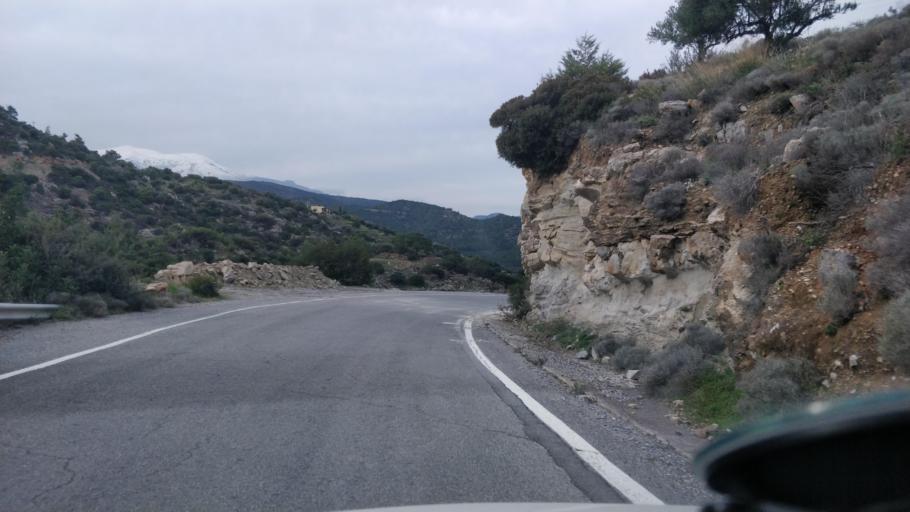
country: GR
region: Crete
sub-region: Nomos Lasithiou
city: Kritsa
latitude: 35.1046
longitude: 25.7116
